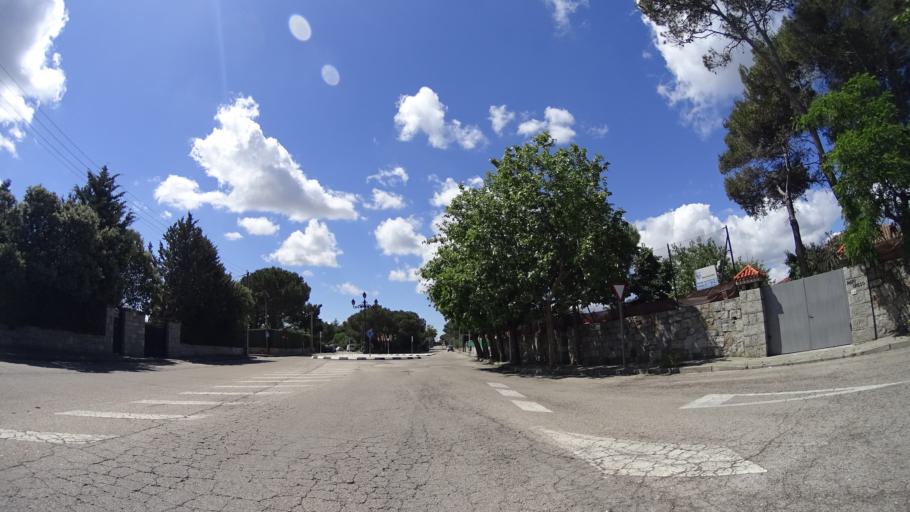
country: ES
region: Madrid
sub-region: Provincia de Madrid
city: Colmenarejo
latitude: 40.5625
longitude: -4.0113
